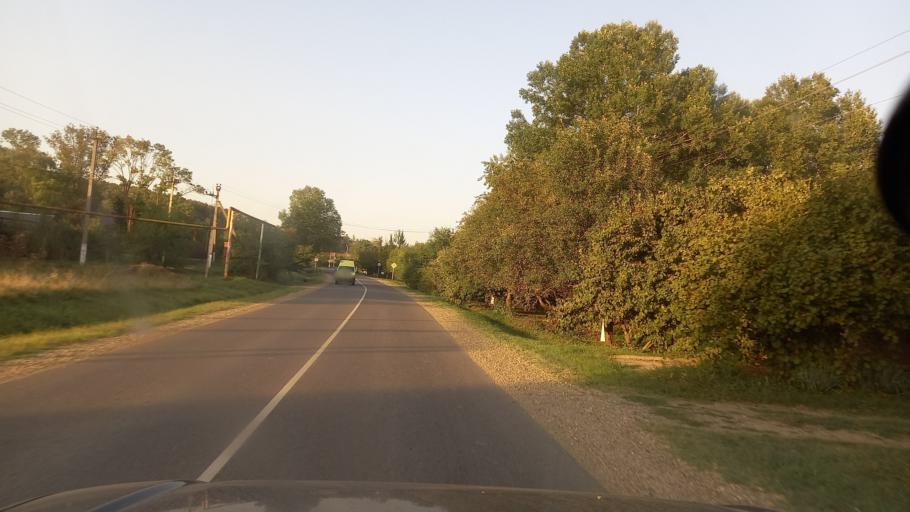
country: RU
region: Krasnodarskiy
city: Smolenskaya
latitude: 44.7659
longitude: 38.7782
